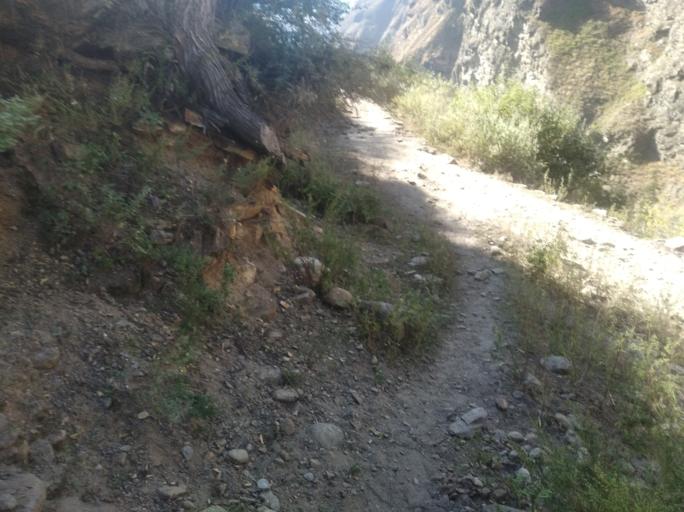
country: NP
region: Western Region
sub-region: Dhawalagiri Zone
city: Jomsom
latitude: 28.8810
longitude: 83.0185
